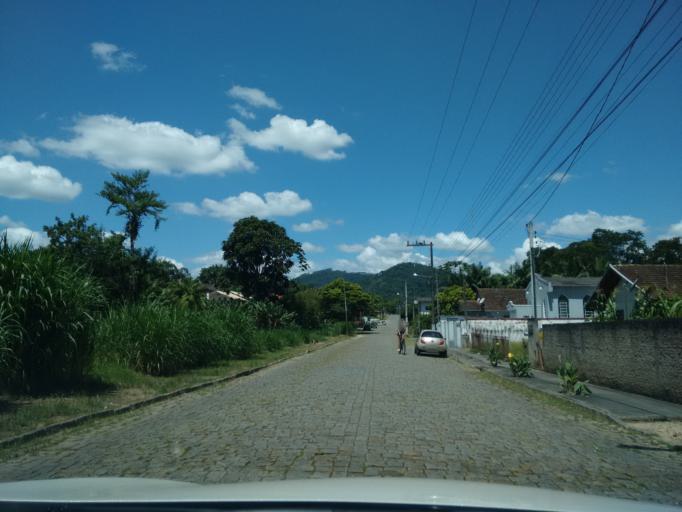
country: BR
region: Santa Catarina
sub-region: Pomerode
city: Pomerode
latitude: -26.7508
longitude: -49.1803
